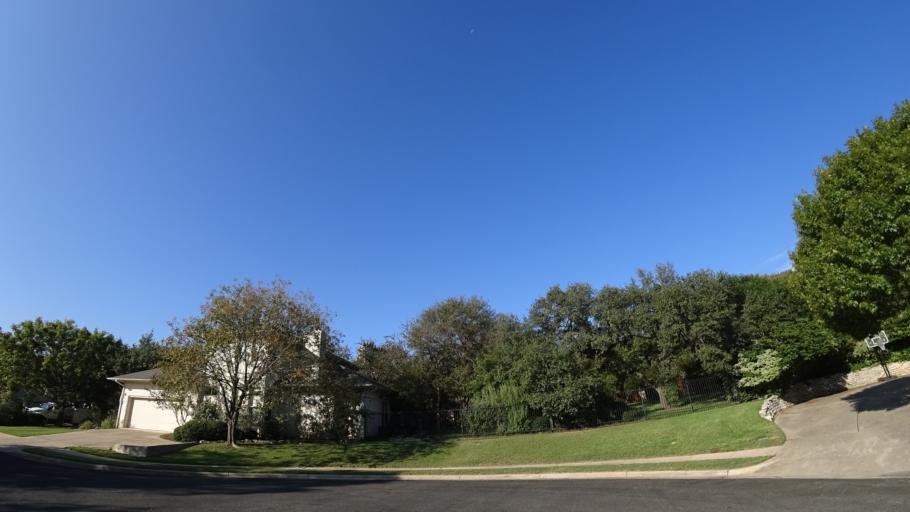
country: US
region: Texas
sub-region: Travis County
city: Rollingwood
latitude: 30.2687
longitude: -97.7965
